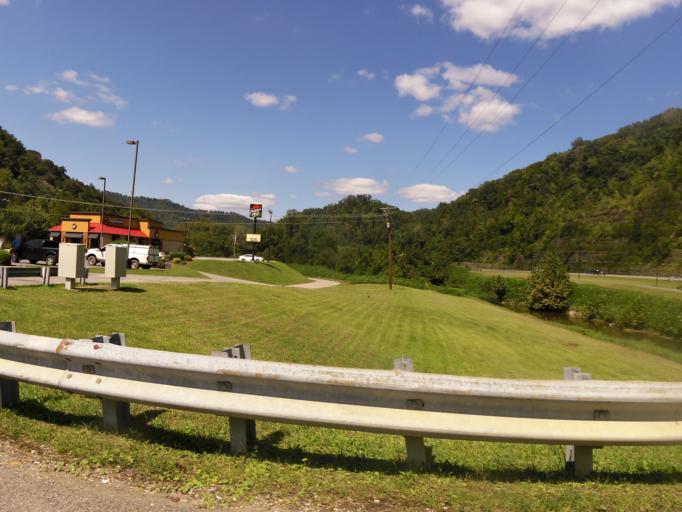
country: US
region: Kentucky
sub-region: Harlan County
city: Harlan
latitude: 36.8210
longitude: -83.3187
